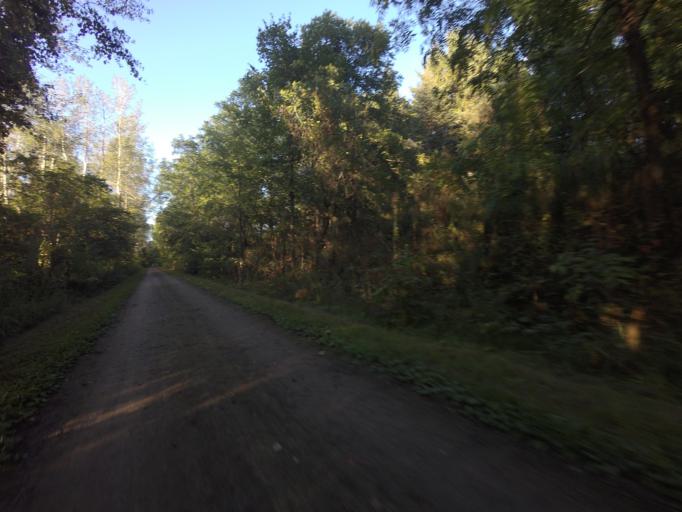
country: CA
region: Ontario
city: Brampton
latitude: 43.8551
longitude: -79.8761
